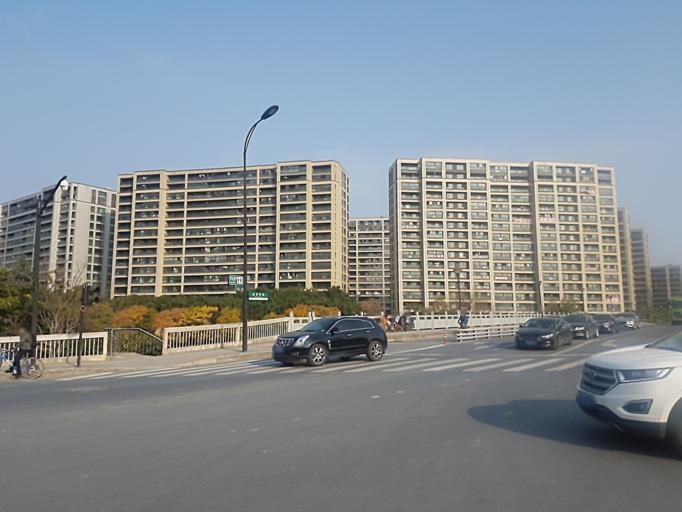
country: CN
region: Zhejiang Sheng
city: Jiangcun
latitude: 30.2982
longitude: 120.0548
